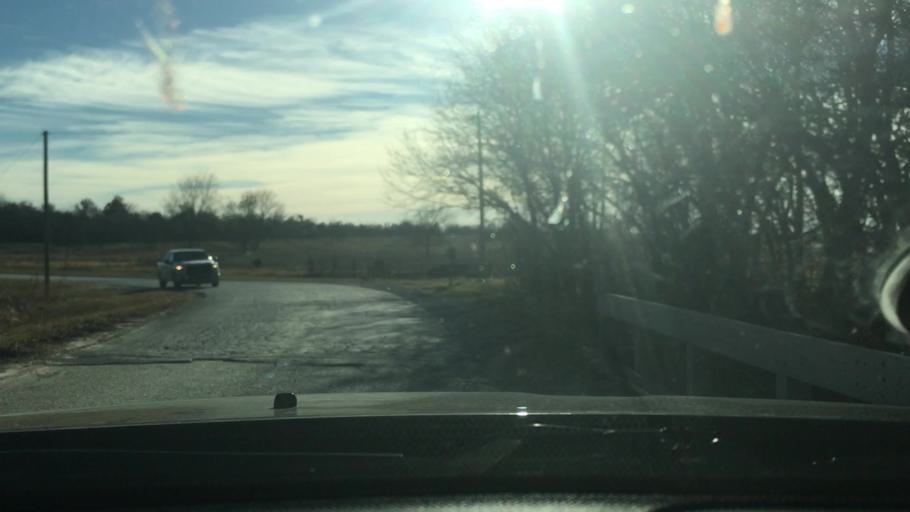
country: US
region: Oklahoma
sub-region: Murray County
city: Davis
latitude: 34.4991
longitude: -97.1582
